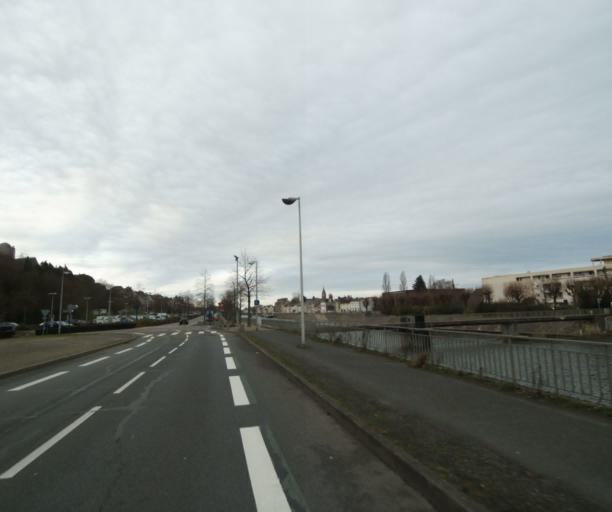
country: FR
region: Pays de la Loire
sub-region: Departement de la Sarthe
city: Coulaines
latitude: 48.0134
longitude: 0.1993
